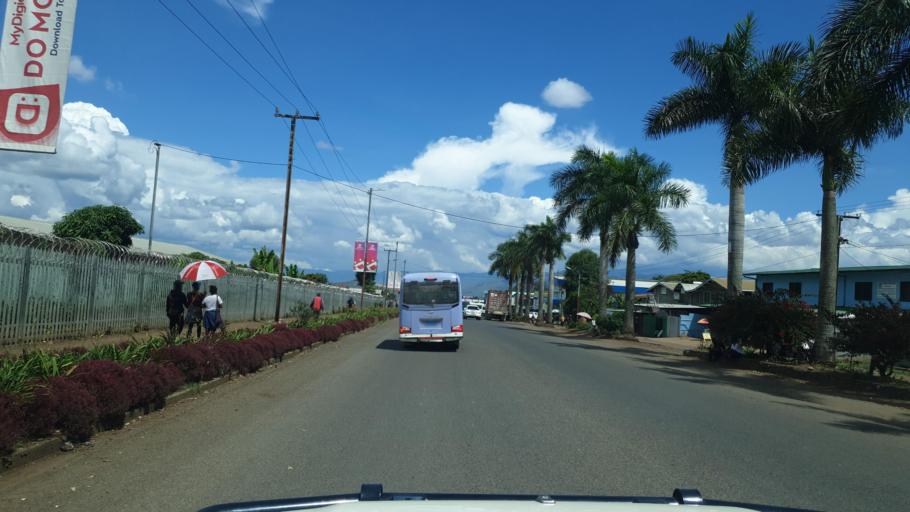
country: PG
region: Eastern Highlands
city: Goroka
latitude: -6.0799
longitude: 145.3895
